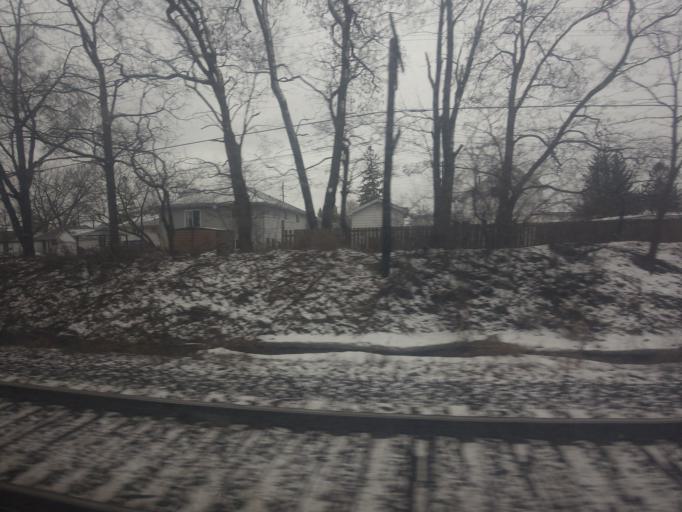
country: CA
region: Ontario
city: Belleville
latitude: 44.1709
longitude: -77.4005
